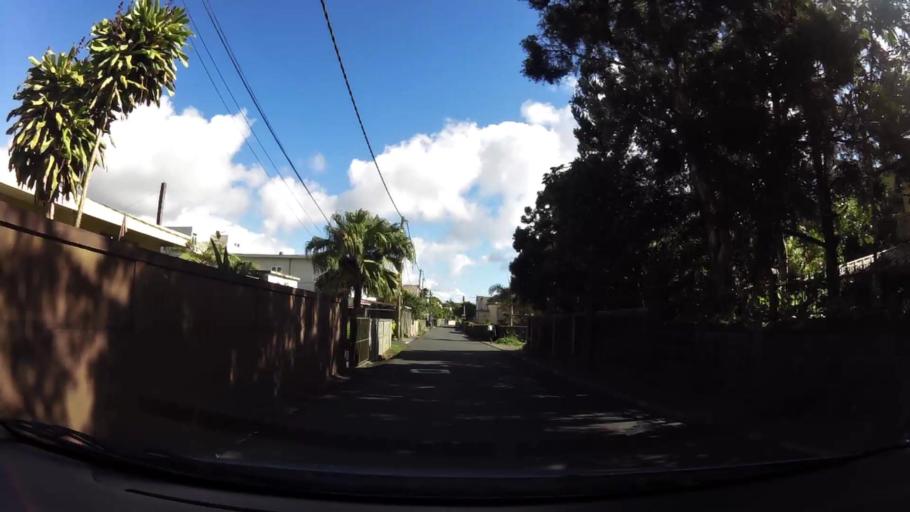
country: MU
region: Plaines Wilhems
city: Curepipe
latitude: -20.3228
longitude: 57.5252
